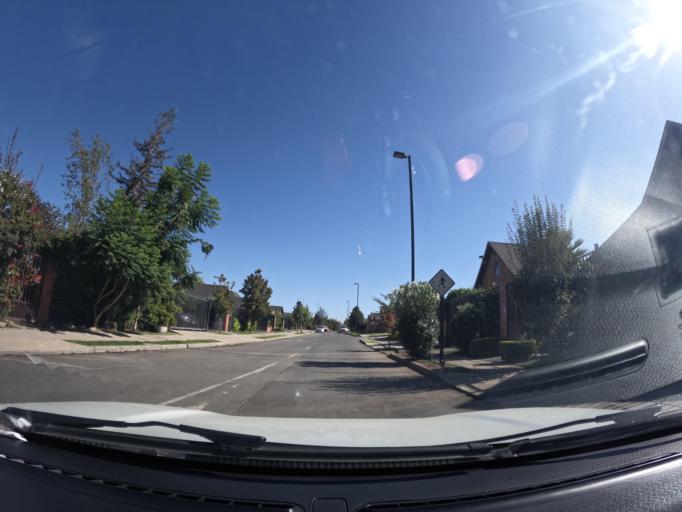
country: CL
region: Santiago Metropolitan
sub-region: Provincia de Santiago
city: Villa Presidente Frei, Nunoa, Santiago, Chile
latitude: -33.5061
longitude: -70.5254
